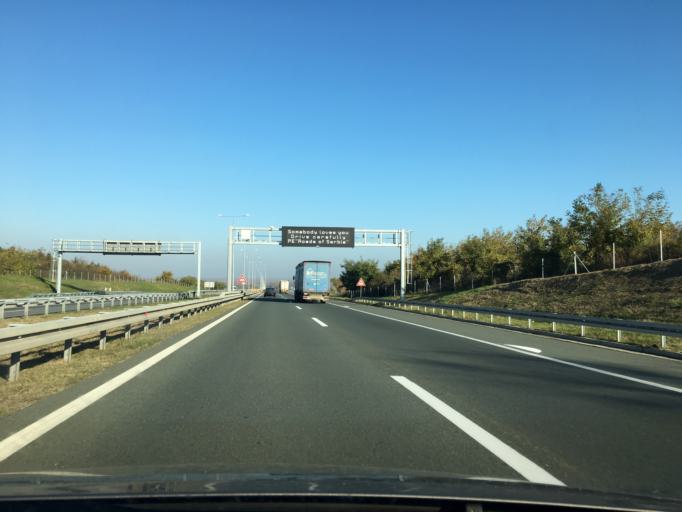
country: RS
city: Beska
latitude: 45.1623
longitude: 20.0810
